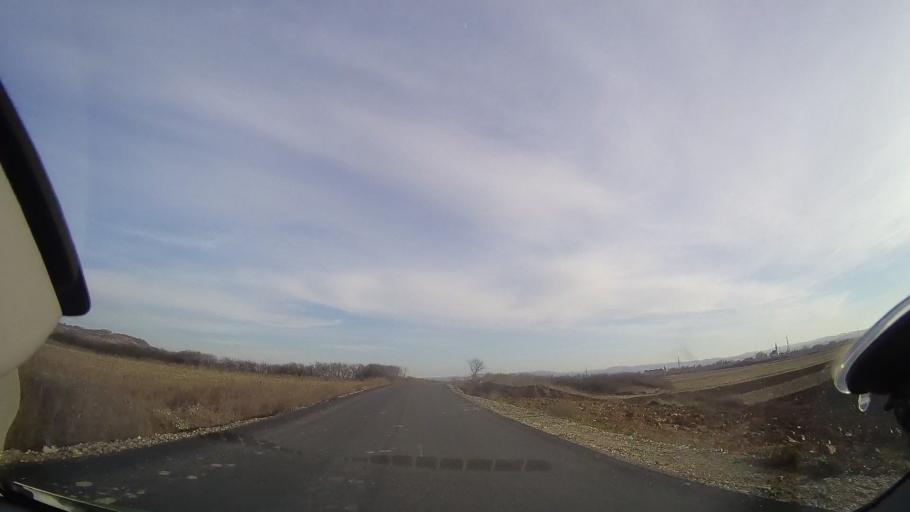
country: RO
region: Bihor
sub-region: Comuna Tileagd
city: Tileagd
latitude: 47.0852
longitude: 22.1838
